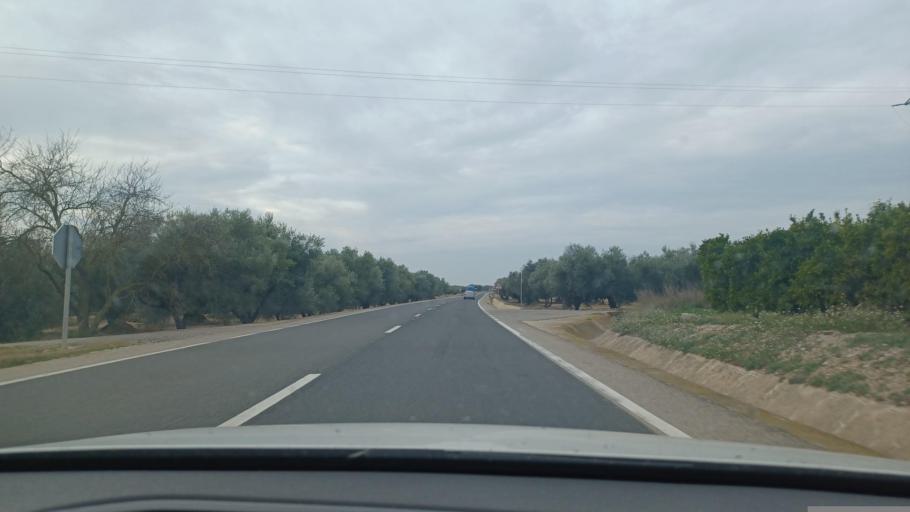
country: ES
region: Catalonia
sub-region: Provincia de Tarragona
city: Santa Barbara
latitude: 40.6713
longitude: 0.4420
